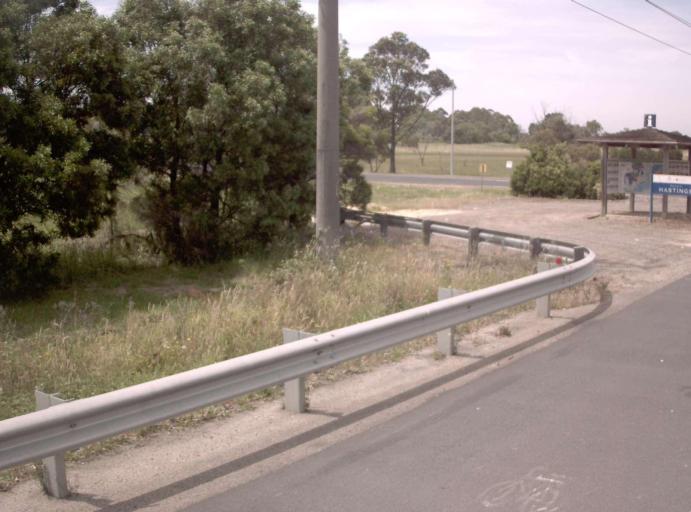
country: AU
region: Victoria
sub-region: Mornington Peninsula
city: Hastings
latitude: -38.2759
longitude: 145.1894
